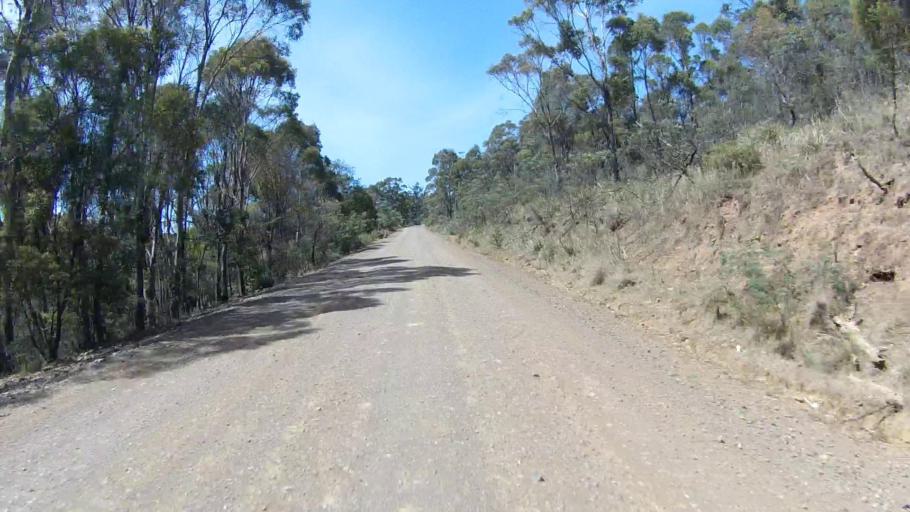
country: AU
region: Tasmania
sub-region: Sorell
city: Sorell
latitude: -42.6457
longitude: 147.7417
